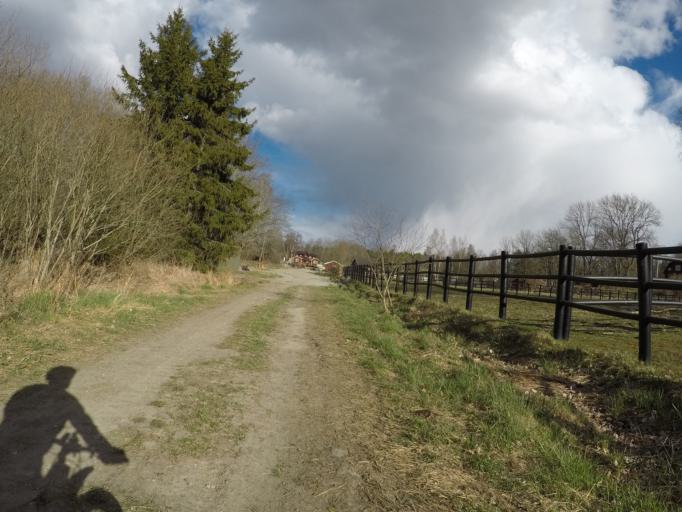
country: SE
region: Soedermanland
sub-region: Eskilstuna Kommun
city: Kvicksund
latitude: 59.4691
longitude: 16.3228
